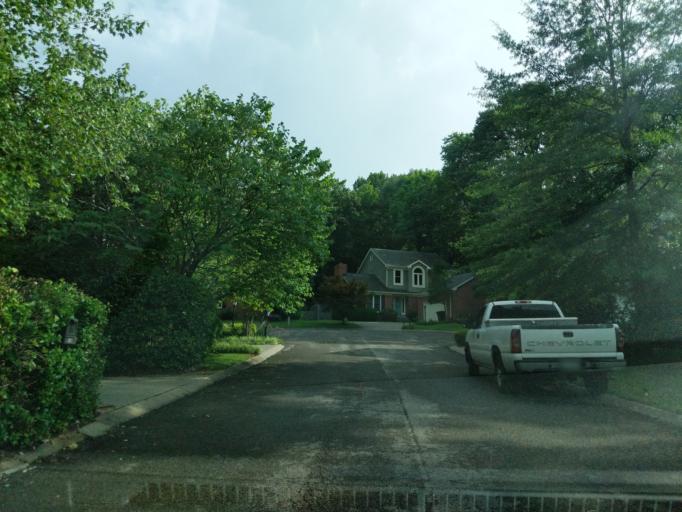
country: US
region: Tennessee
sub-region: Cheatham County
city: Pegram
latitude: 36.0277
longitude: -86.9565
